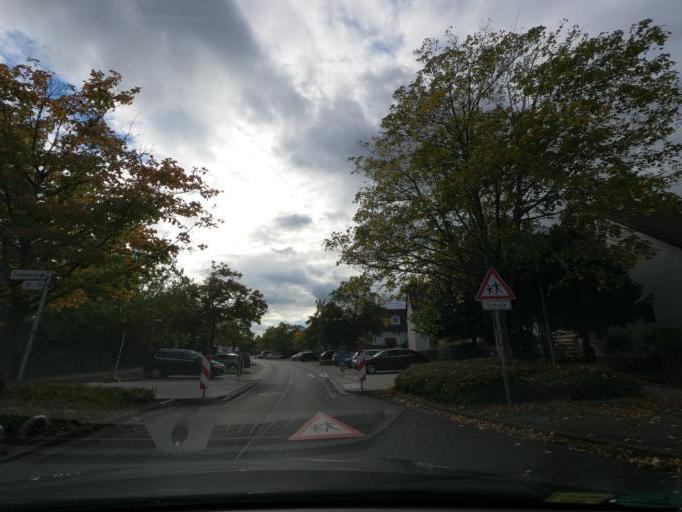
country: DE
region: Lower Saxony
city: Leiferde
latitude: 52.2186
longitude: 10.5181
